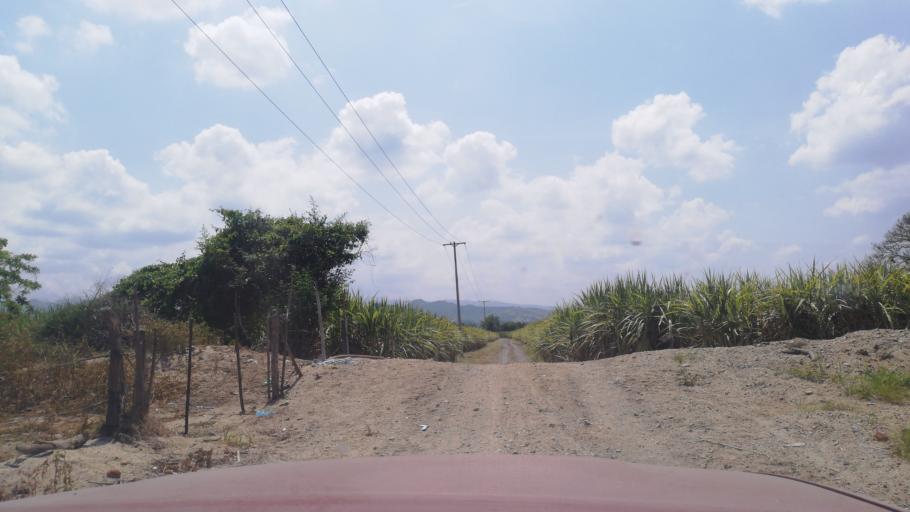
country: CO
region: Valle del Cauca
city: San Pedro
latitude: 3.9902
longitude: -76.2643
